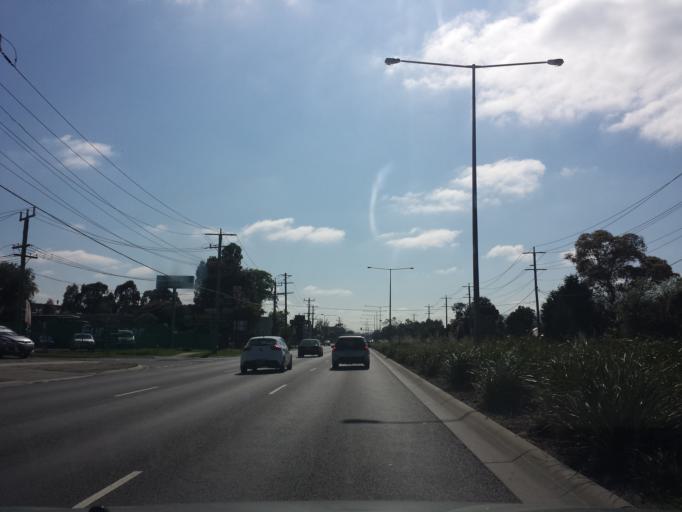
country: AU
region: Victoria
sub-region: Maroondah
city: Croydon South
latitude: -37.8298
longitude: 145.2763
